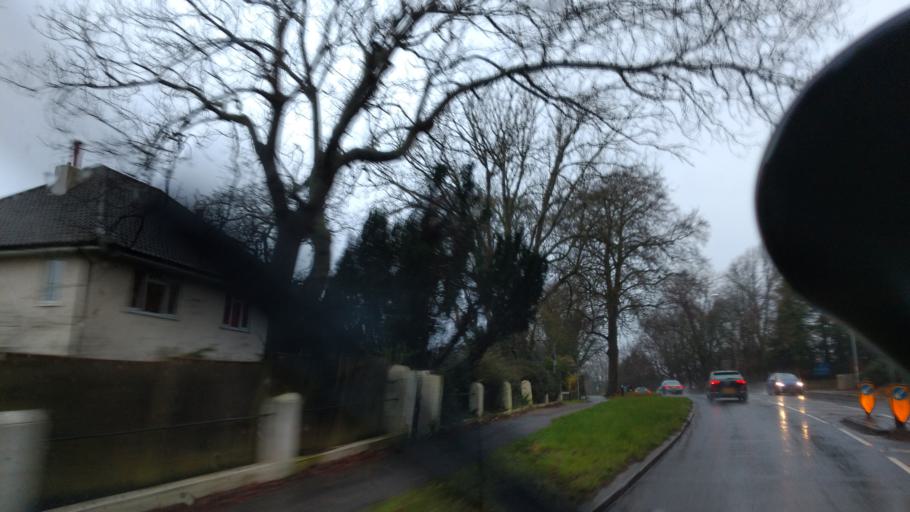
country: GB
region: England
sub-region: West Sussex
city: Broadwater
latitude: 50.8377
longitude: -0.3881
